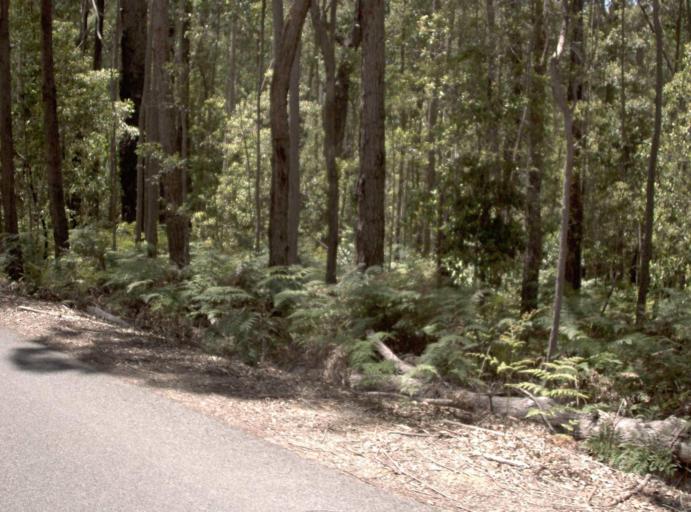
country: AU
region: New South Wales
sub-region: Bombala
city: Bombala
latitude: -37.4863
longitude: 148.9305
